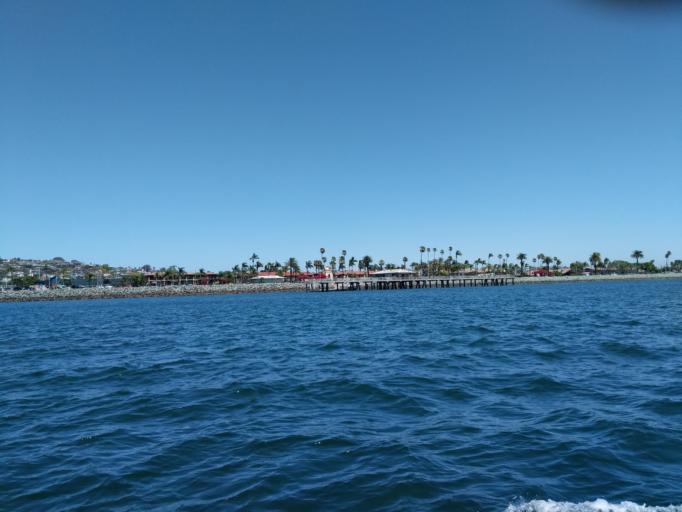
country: US
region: California
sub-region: San Diego County
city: Coronado
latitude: 32.7096
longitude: -117.2278
